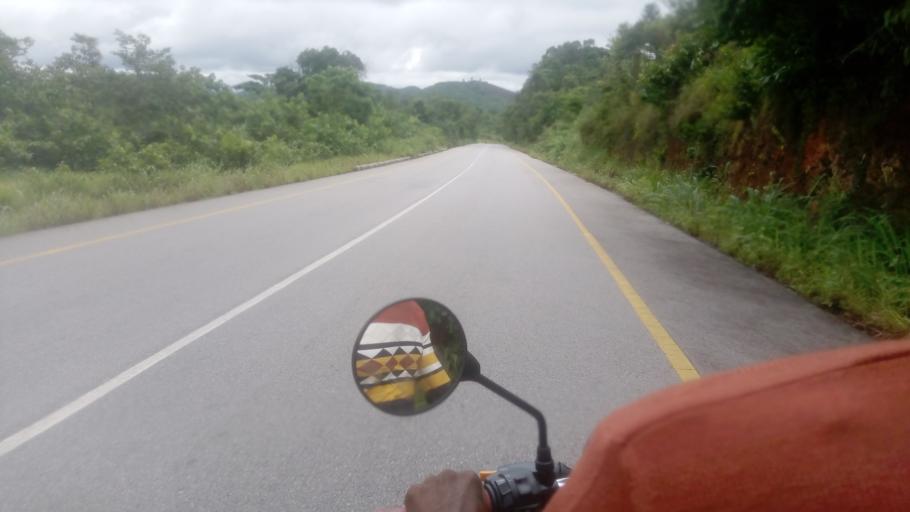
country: SL
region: Northern Province
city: Masaka
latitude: 8.6454
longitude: -11.7530
